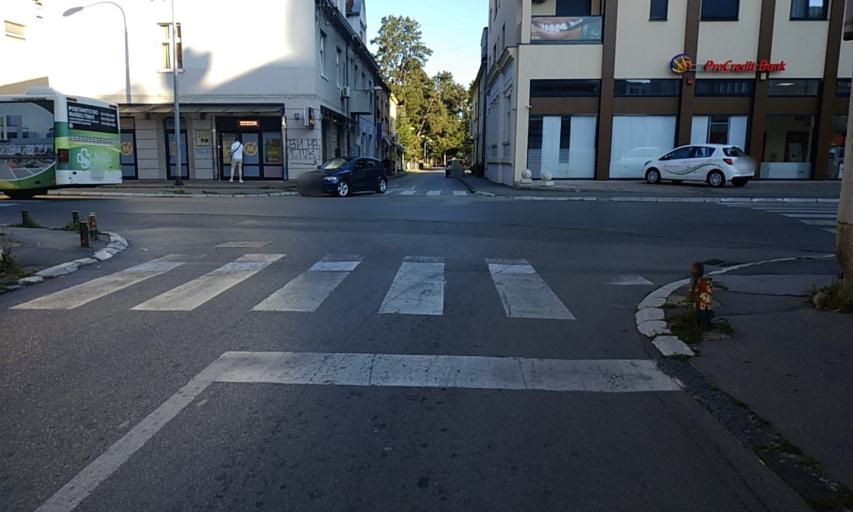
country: BA
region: Republika Srpska
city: Banja Luka
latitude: 44.7779
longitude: 17.1946
